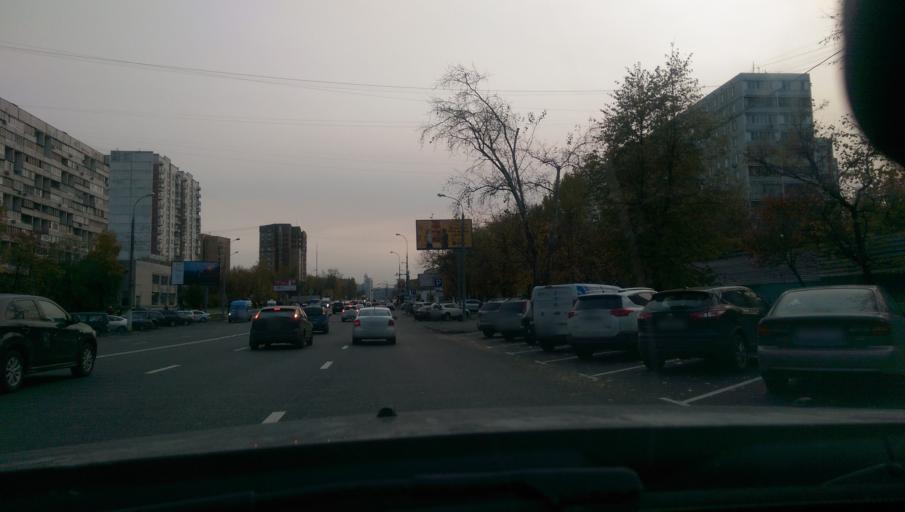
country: RU
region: Moscow
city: Leonovo
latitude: 55.8724
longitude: 37.6658
